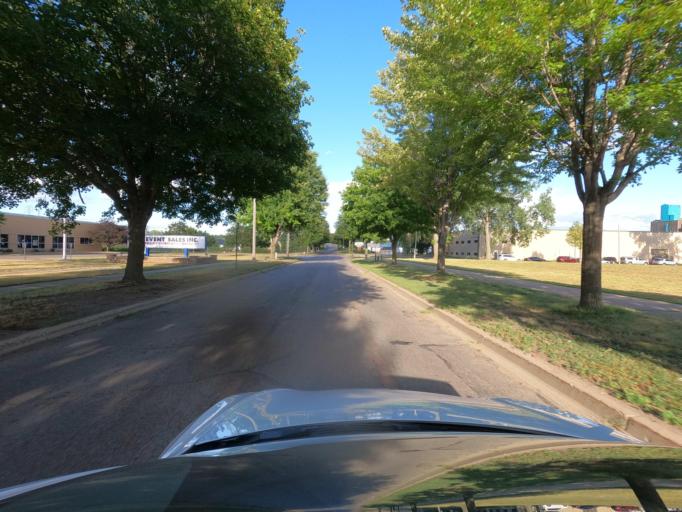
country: US
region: Minnesota
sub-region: Anoka County
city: Columbia Heights
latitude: 45.0276
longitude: -93.2737
